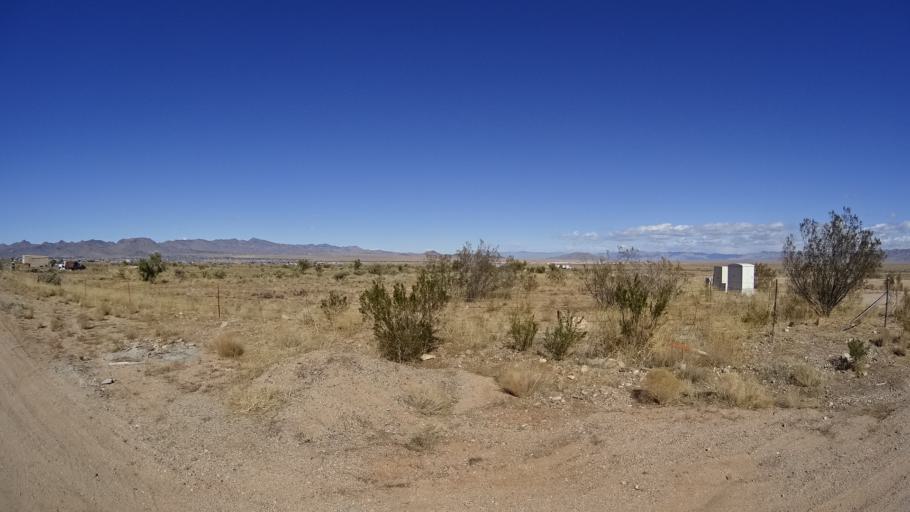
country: US
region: Arizona
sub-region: Mohave County
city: Kingman
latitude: 35.2035
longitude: -113.9584
